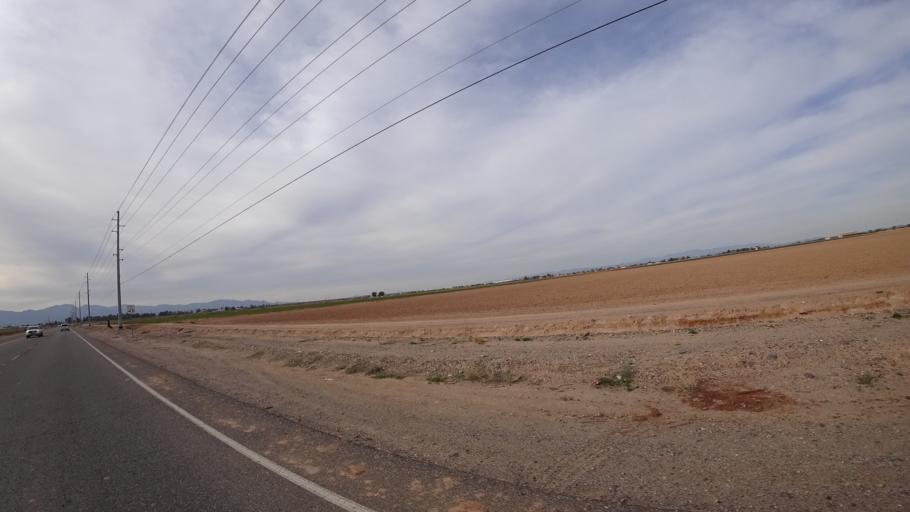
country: US
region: Arizona
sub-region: Maricopa County
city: Youngtown
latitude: 33.5655
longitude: -112.3320
